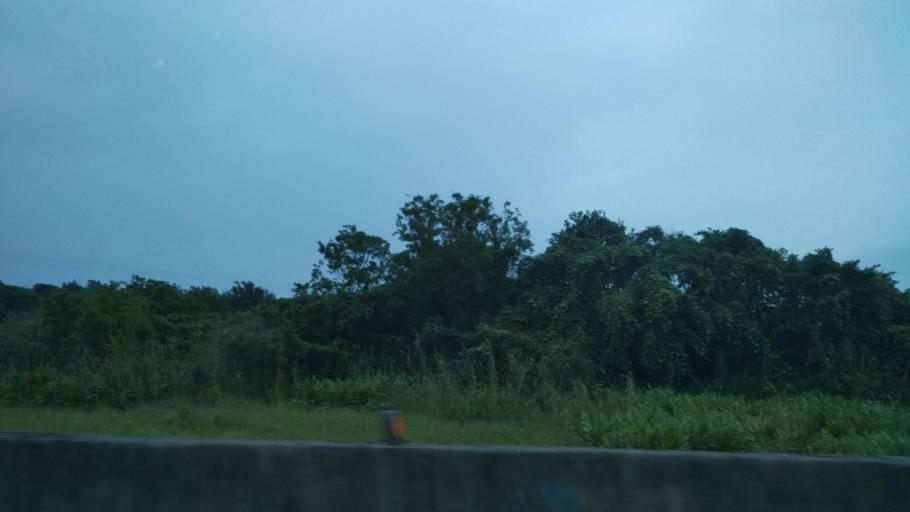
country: TW
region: Taiwan
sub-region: Keelung
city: Keelung
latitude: 25.2097
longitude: 121.6501
